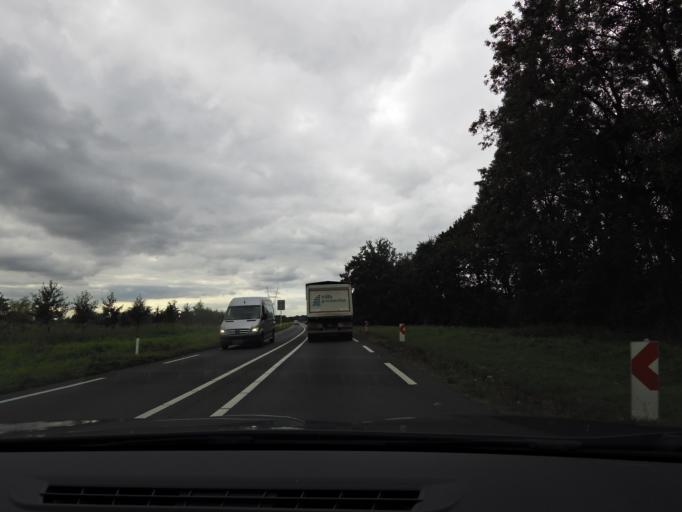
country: NL
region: South Holland
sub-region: Gemeente Krimpen aan den IJssel
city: Krimpen aan den IJssel
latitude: 51.9081
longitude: 4.6195
